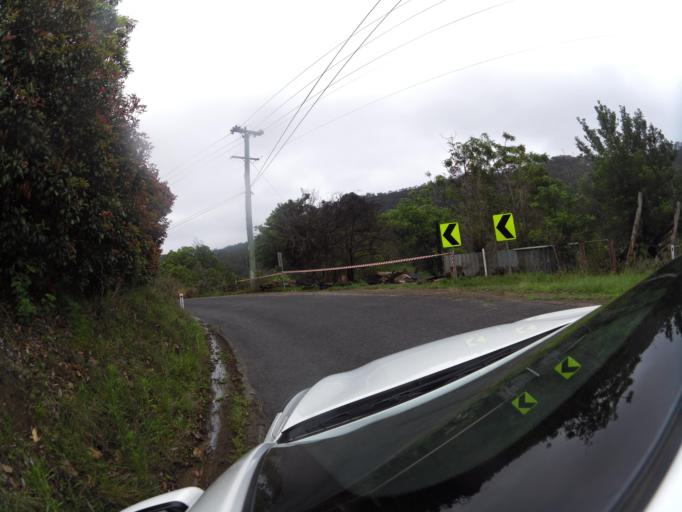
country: AU
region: New South Wales
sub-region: Hornsby Shire
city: Glenorie
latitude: -33.4163
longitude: 150.9540
